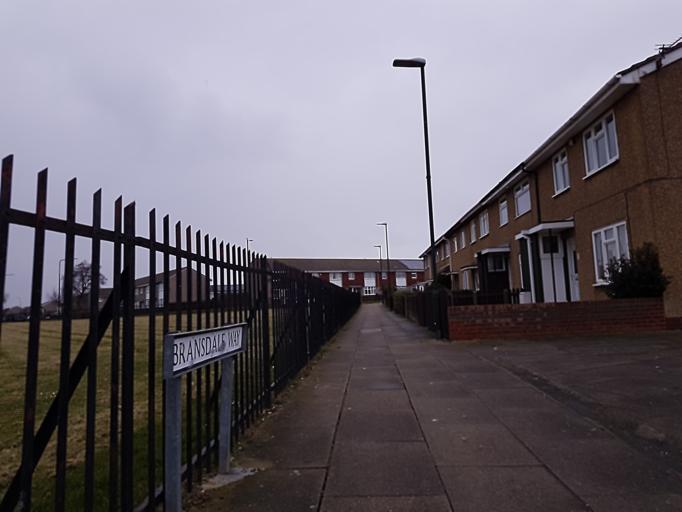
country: GB
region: England
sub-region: North East Lincolnshire
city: Great Coates
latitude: 53.5677
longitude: -0.1224
